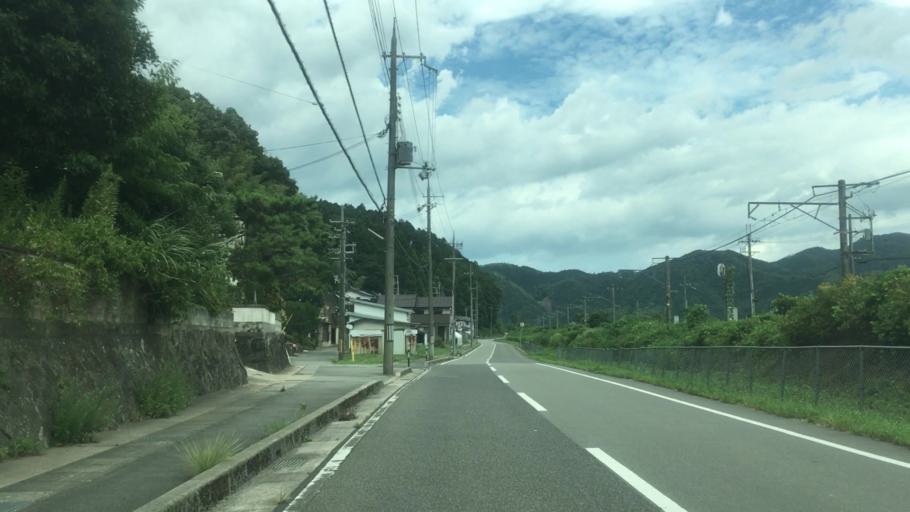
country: JP
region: Hyogo
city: Toyooka
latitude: 35.5686
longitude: 134.8040
